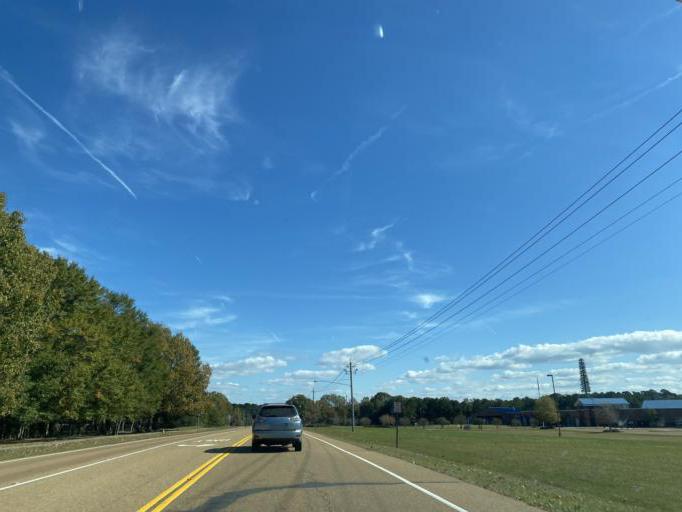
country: US
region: Mississippi
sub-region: Madison County
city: Madison
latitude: 32.4575
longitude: -90.0940
